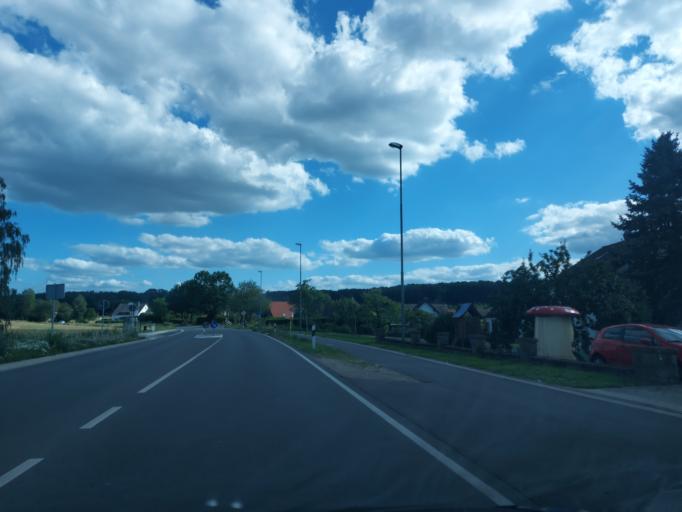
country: DE
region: Lower Saxony
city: Hilter
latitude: 52.1286
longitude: 8.1534
